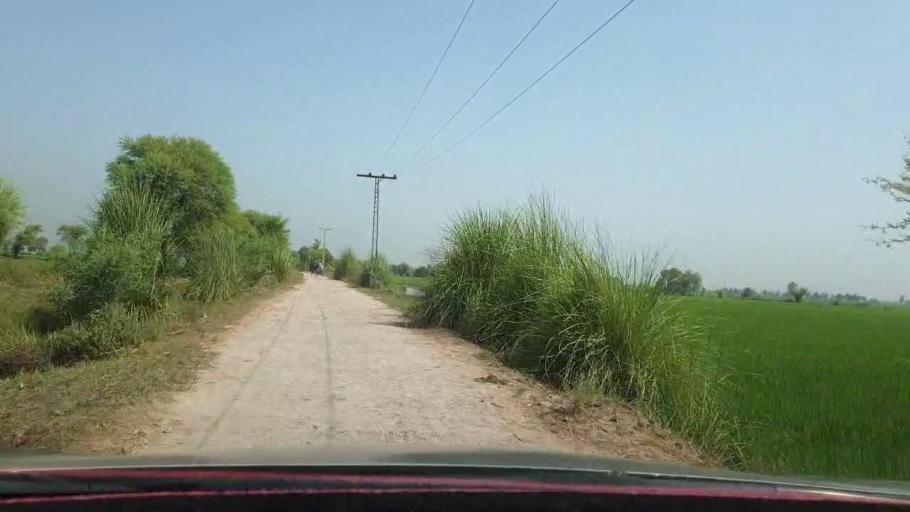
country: PK
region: Sindh
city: Warah
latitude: 27.4903
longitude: 67.8350
